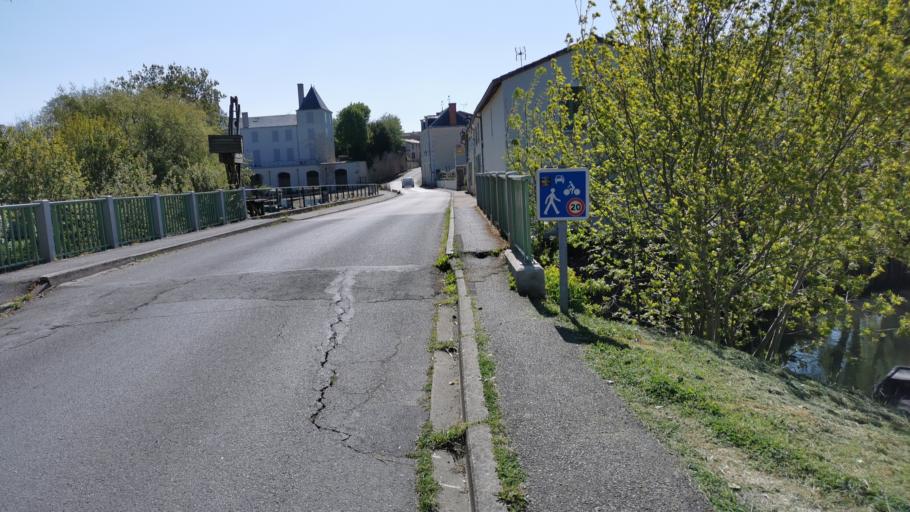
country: FR
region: Poitou-Charentes
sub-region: Departement des Deux-Sevres
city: Saint-Hilaire-la-Palud
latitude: 46.2982
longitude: -0.6938
